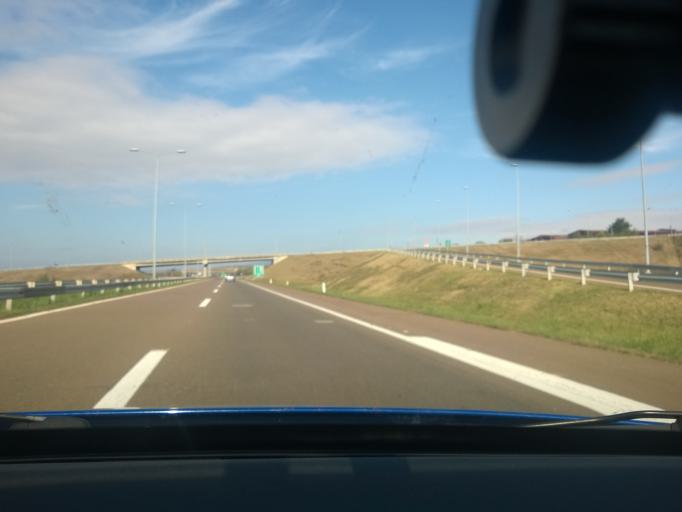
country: RS
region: Central Serbia
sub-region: Nisavski Okrug
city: Aleksinac
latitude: 43.5494
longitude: 21.6872
